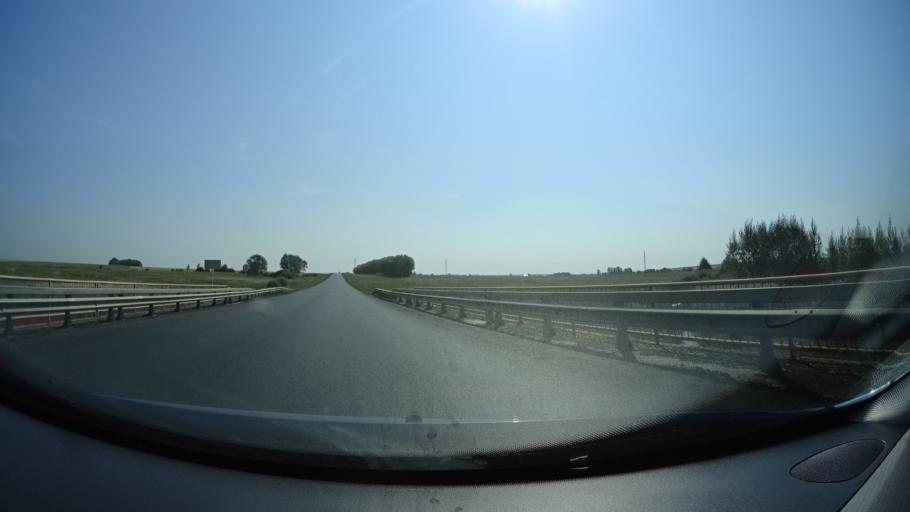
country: RU
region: Bashkortostan
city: Kabakovo
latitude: 54.4372
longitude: 56.0054
